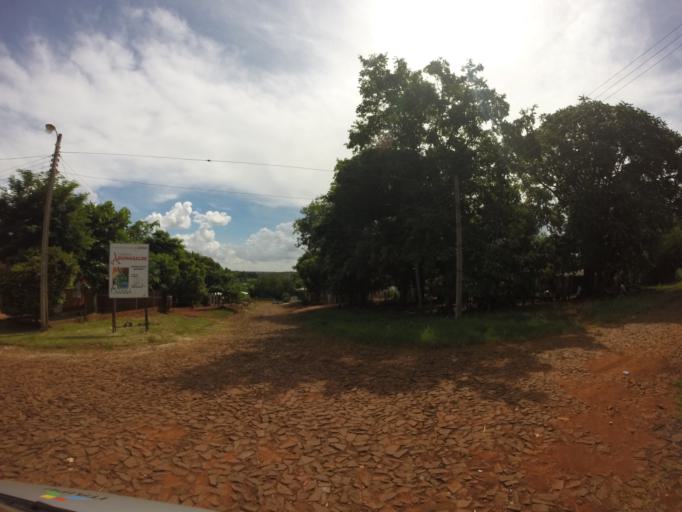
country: PY
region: Alto Parana
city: Ciudad del Este
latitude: -25.4406
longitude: -54.6427
